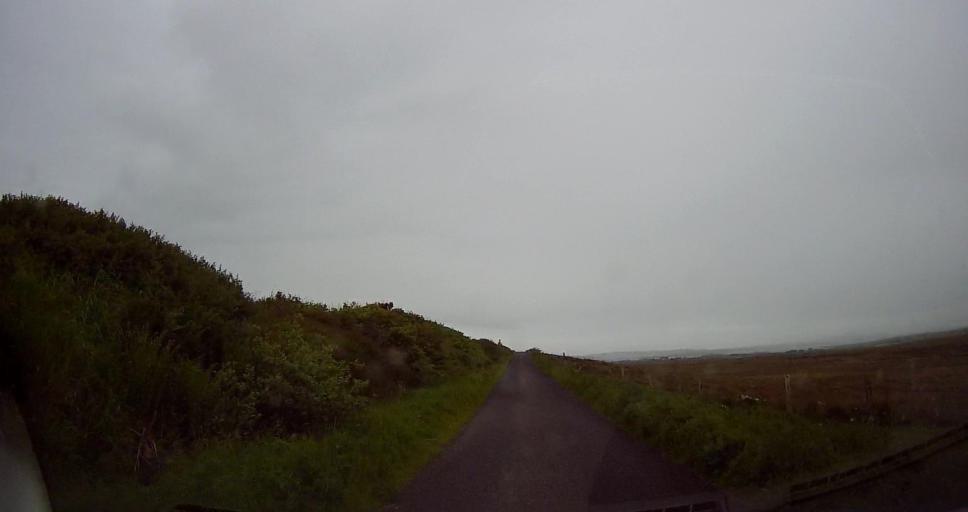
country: GB
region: Scotland
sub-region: Orkney Islands
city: Stromness
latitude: 58.9771
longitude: -3.1655
